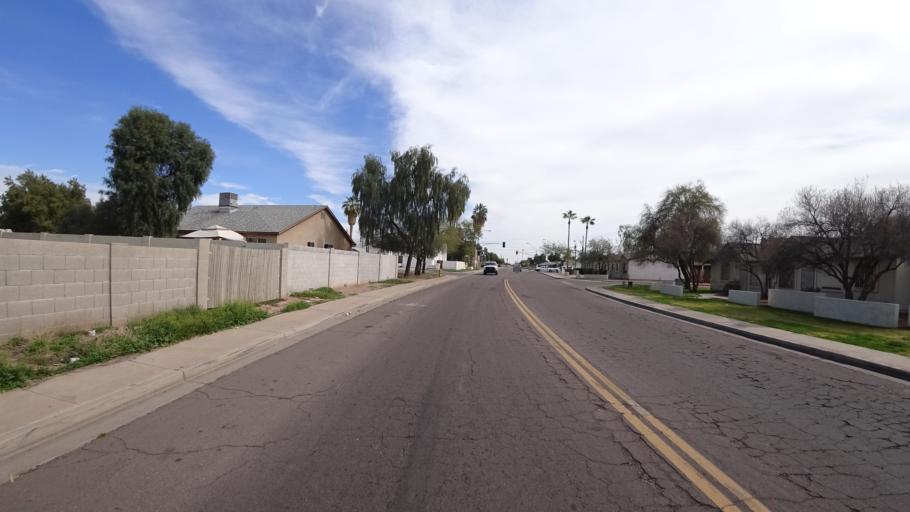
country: US
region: Arizona
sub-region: Maricopa County
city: Glendale
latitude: 33.4876
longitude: -112.2042
